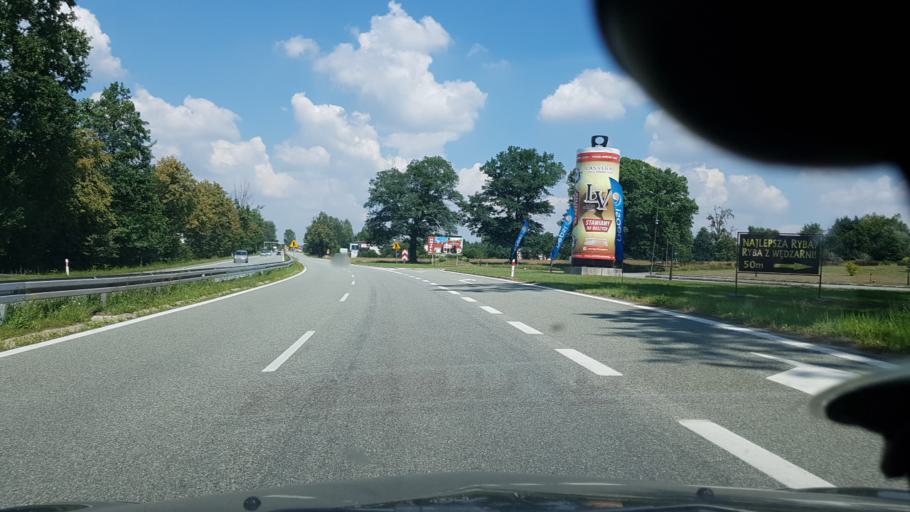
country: PL
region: Silesian Voivodeship
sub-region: Powiat pszczynski
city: Rudziczka
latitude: 50.0797
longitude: 18.7527
